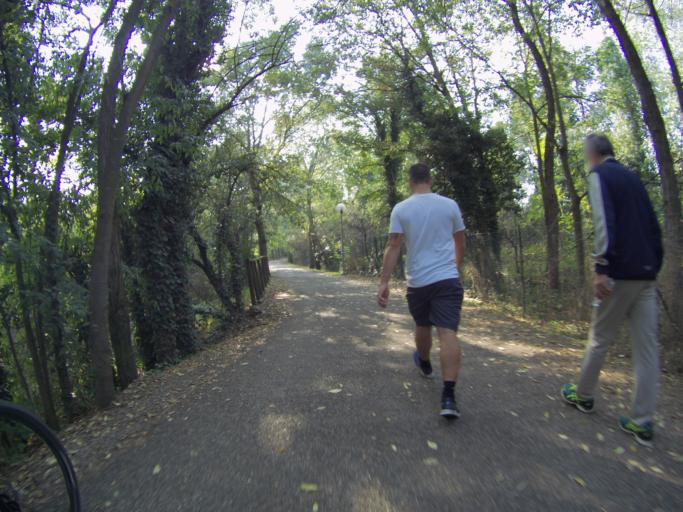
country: IT
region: Emilia-Romagna
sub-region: Provincia di Reggio Emilia
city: Reggio nell'Emilia
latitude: 44.6722
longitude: 10.6140
